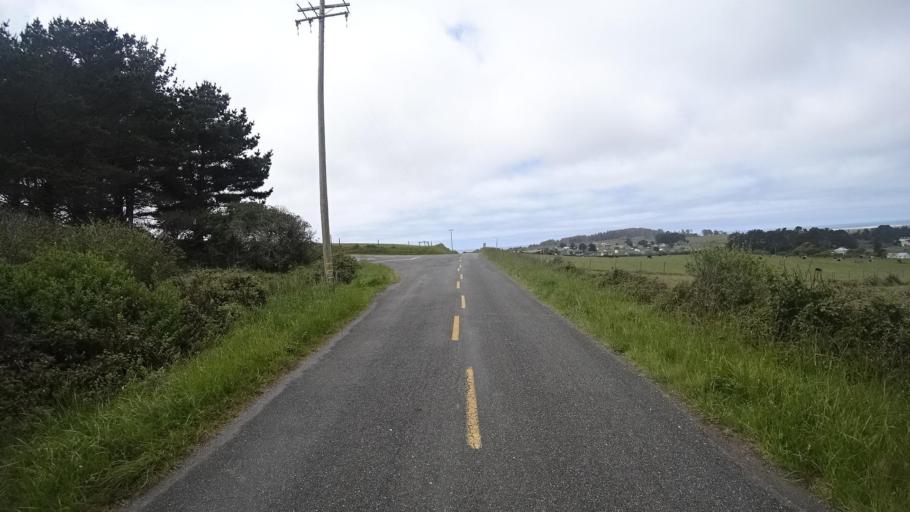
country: US
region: California
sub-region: Humboldt County
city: Humboldt Hill
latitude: 40.6868
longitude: -124.2450
